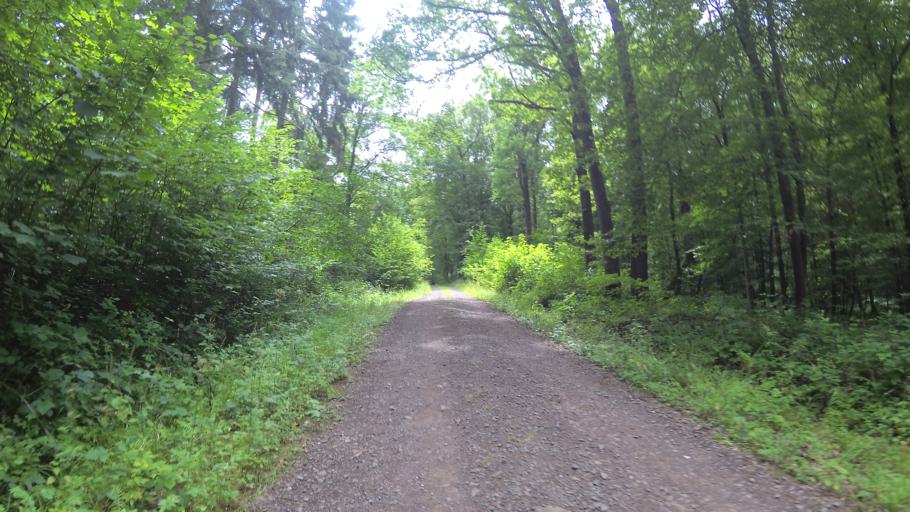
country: DE
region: Saarland
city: Ottweiler
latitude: 49.4192
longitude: 7.1446
